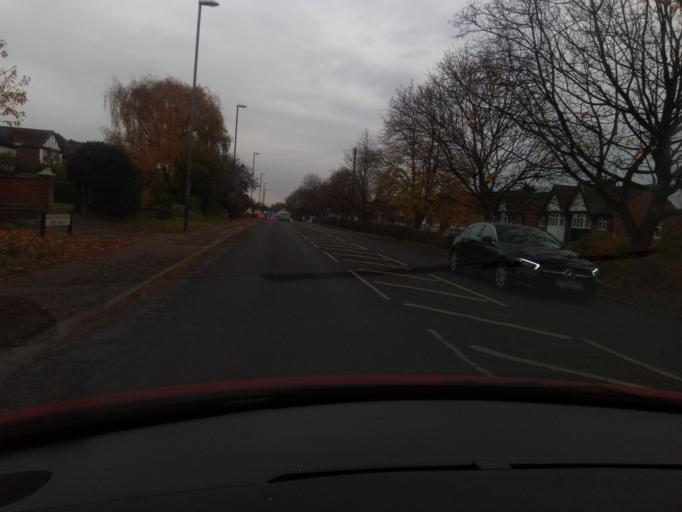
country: GB
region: England
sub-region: Derbyshire
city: Borrowash
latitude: 52.9202
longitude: -1.4279
